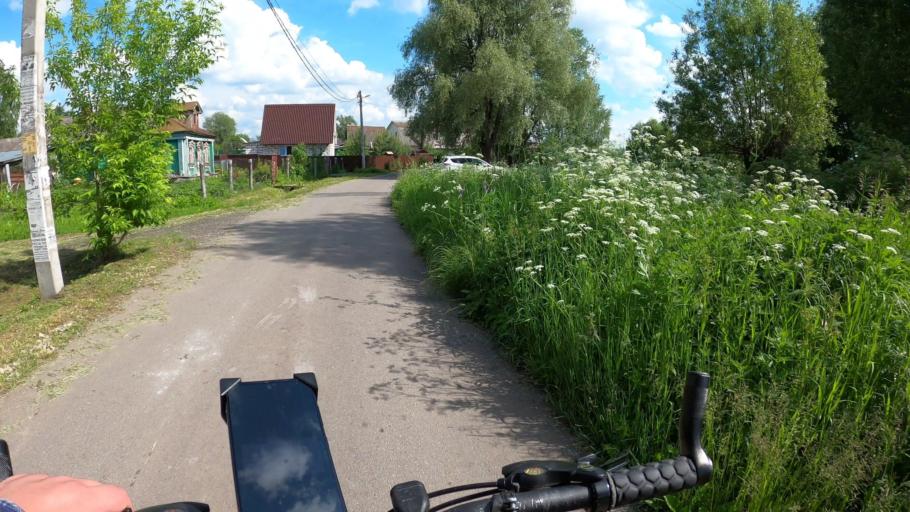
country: RU
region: Moskovskaya
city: Konobeyevo
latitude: 55.3934
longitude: 38.6829
